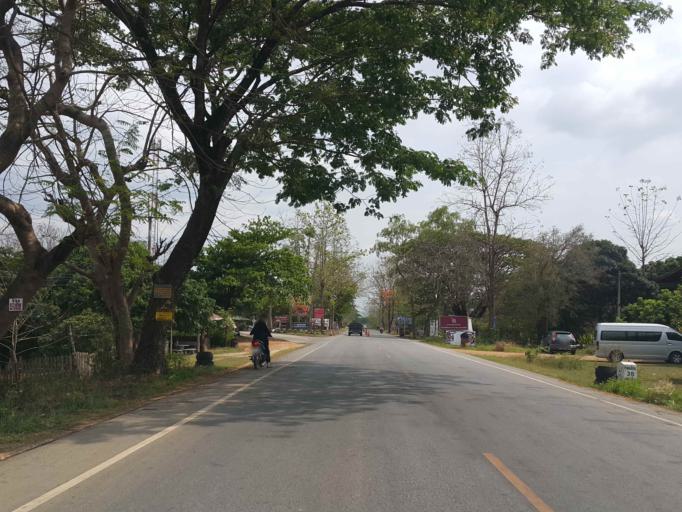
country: TH
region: Lampang
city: Thoen
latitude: 17.5116
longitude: 99.3506
